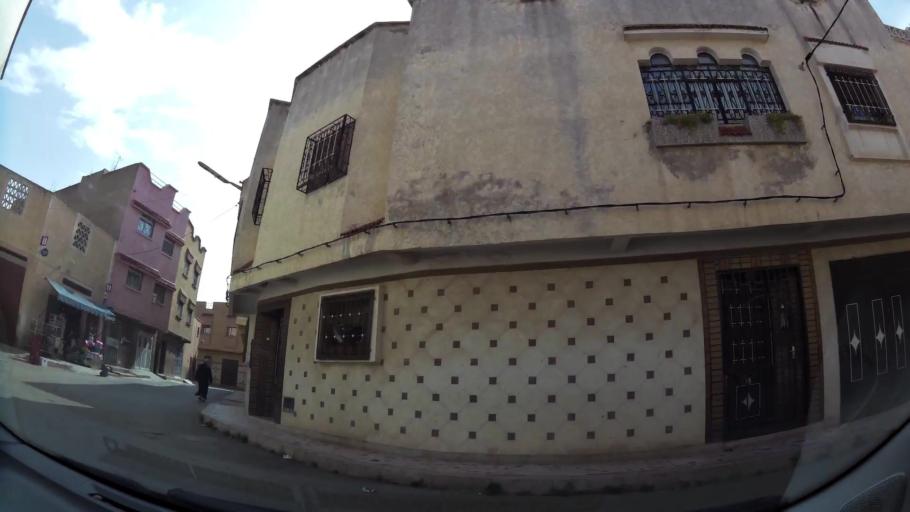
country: MA
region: Oriental
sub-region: Oujda-Angad
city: Oujda
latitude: 34.6890
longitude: -1.9050
